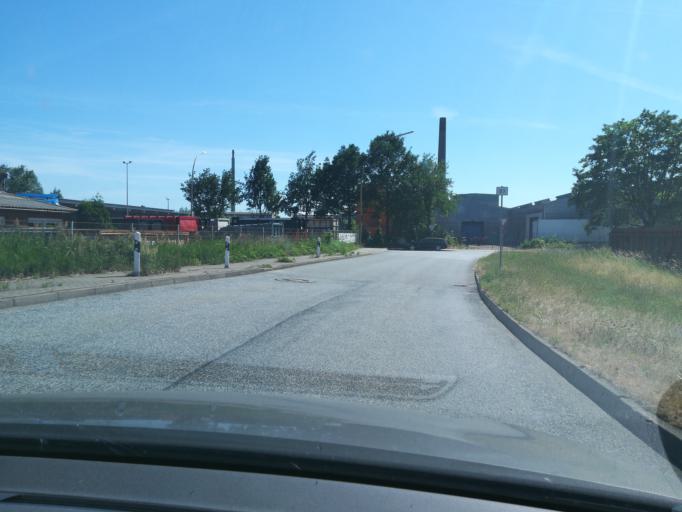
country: DE
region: Hamburg
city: Rothenburgsort
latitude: 53.5223
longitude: 10.0432
